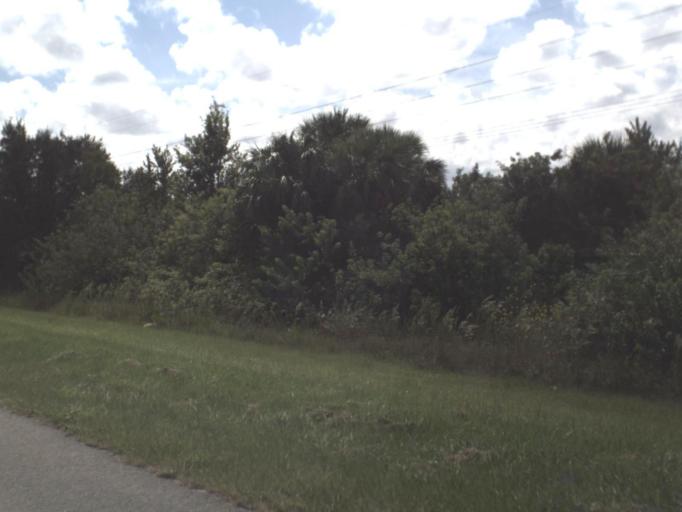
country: US
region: Florida
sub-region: Collier County
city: Immokalee
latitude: 26.3837
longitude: -81.3700
